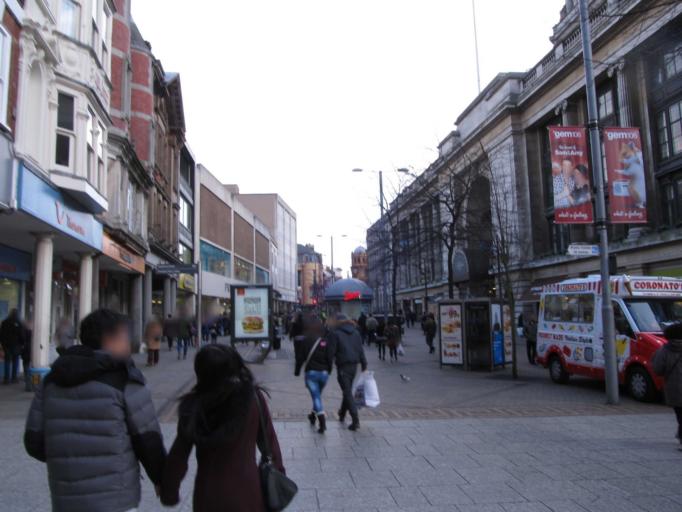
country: GB
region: England
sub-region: Nottingham
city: Nottingham
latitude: 52.9537
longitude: -1.1494
